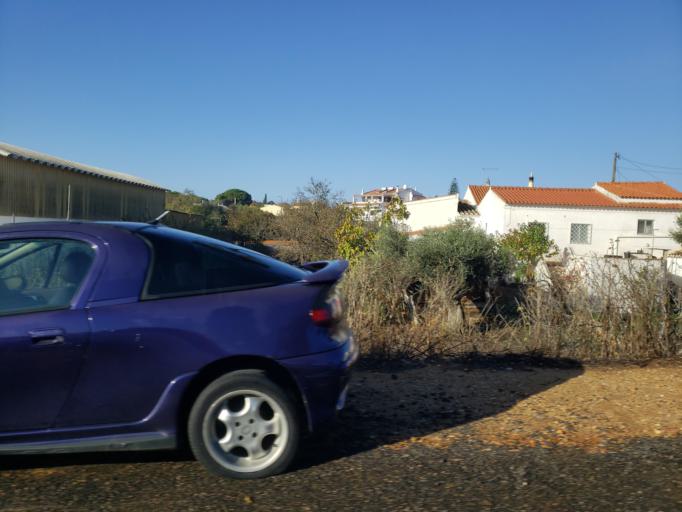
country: PT
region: Faro
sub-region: Portimao
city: Portimao
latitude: 37.1551
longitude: -8.5604
